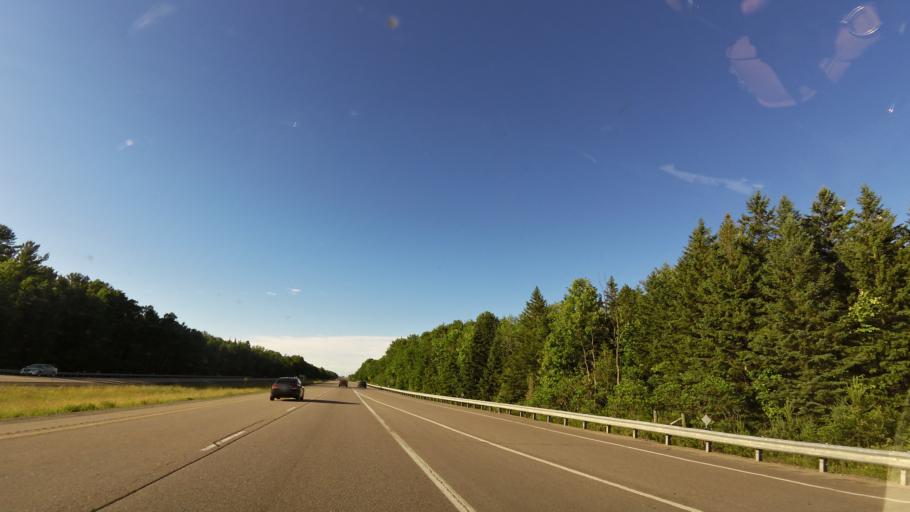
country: CA
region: Ontario
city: Barrie
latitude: 44.6279
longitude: -79.6584
